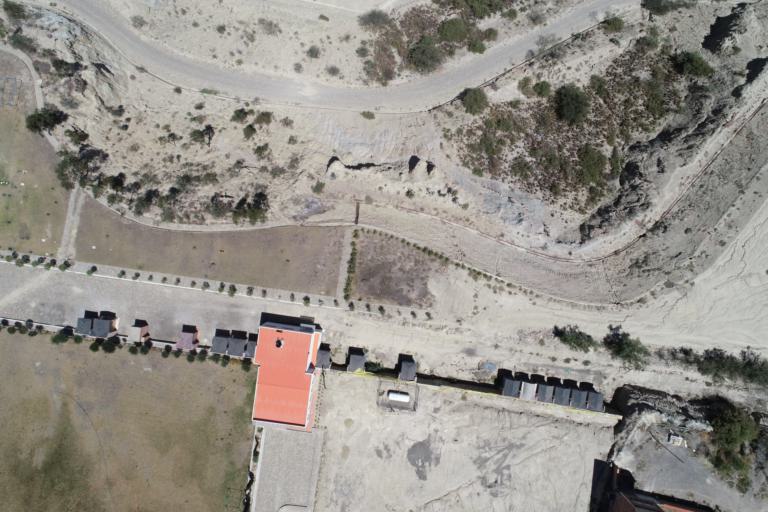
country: BO
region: La Paz
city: La Paz
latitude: -16.6180
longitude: -68.0592
